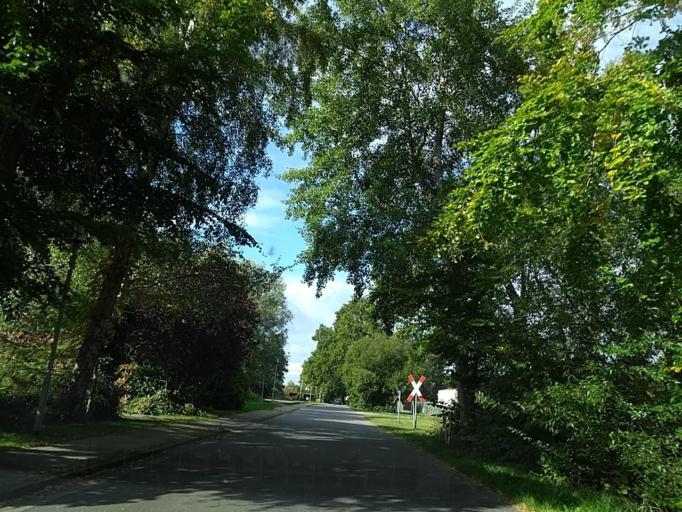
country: DE
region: Mecklenburg-Vorpommern
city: Rovershagen
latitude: 54.1825
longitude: 12.2585
